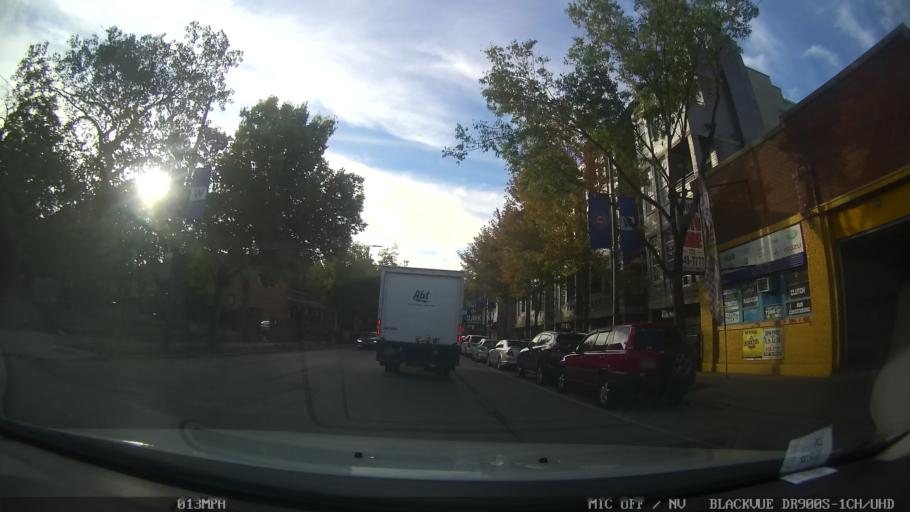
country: US
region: Illinois
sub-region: Cook County
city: Lincolnwood
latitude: 41.9523
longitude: -87.6607
